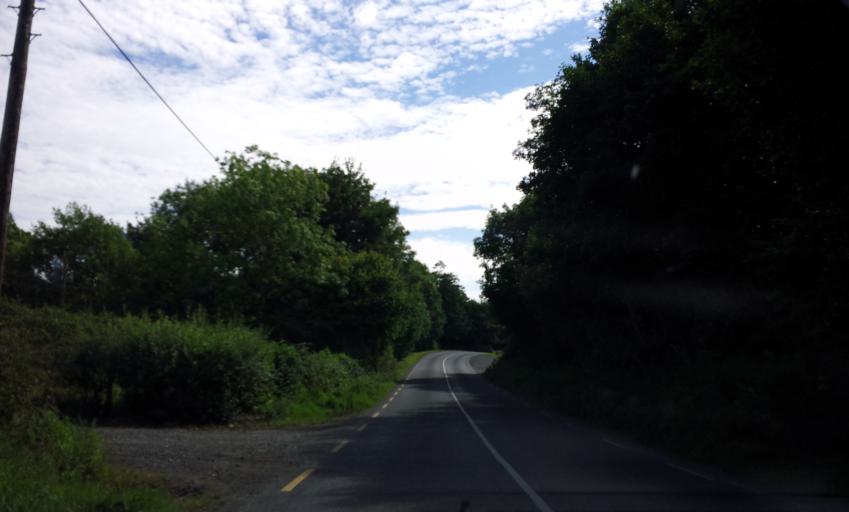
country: IE
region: Leinster
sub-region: Laois
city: Stradbally
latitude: 52.9686
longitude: -7.2096
